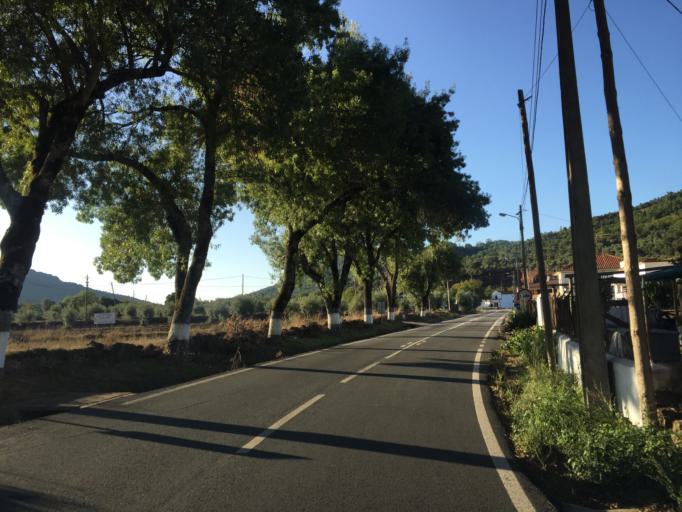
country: PT
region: Portalegre
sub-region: Marvao
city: Marvao
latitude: 39.3846
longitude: -7.3982
